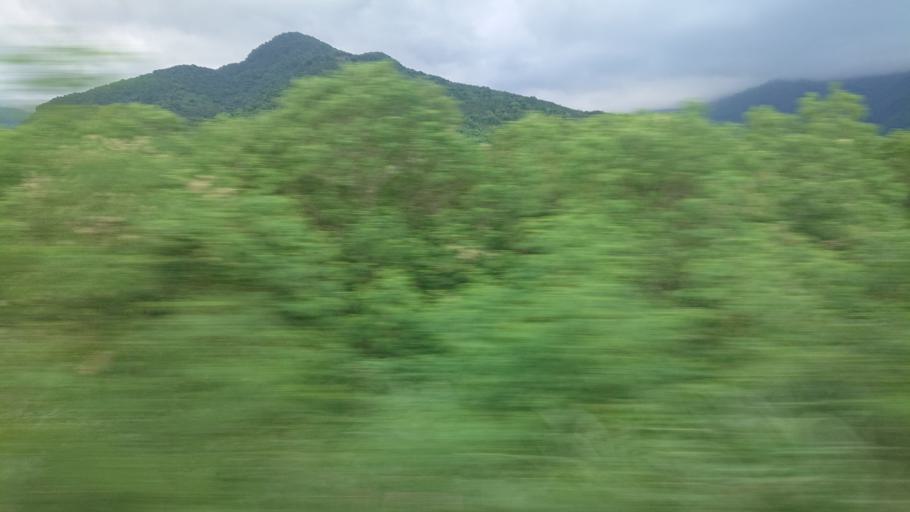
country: TW
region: Taiwan
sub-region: Hualien
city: Hualian
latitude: 23.6208
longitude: 121.3961
